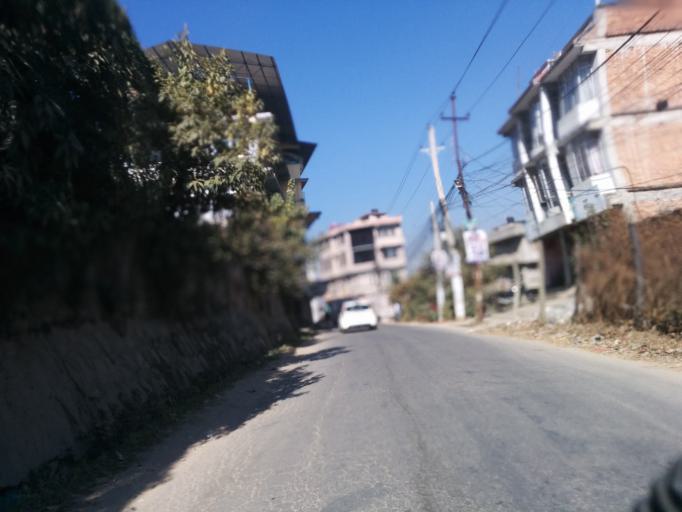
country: NP
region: Central Region
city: Kirtipur
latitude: 27.6780
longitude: 85.2800
